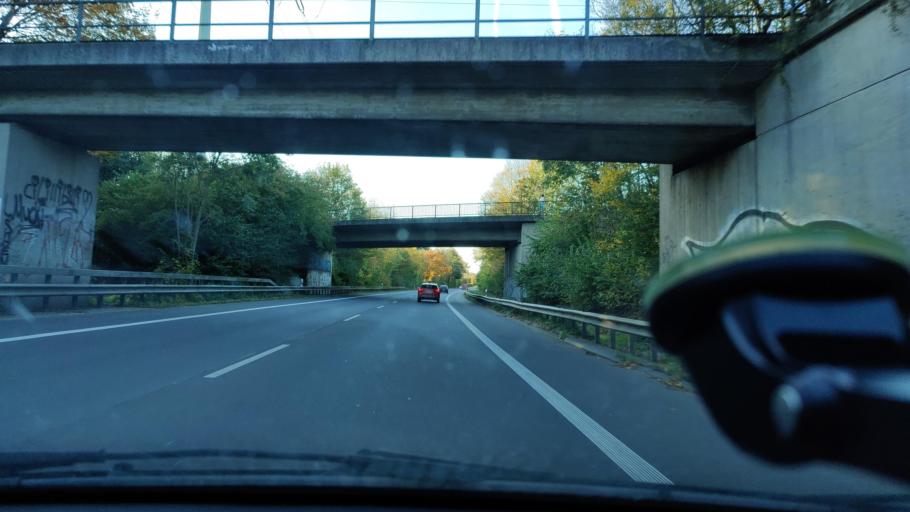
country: DE
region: North Rhine-Westphalia
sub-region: Regierungsbezirk Dusseldorf
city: Monchengladbach
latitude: 51.2290
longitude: 6.4670
